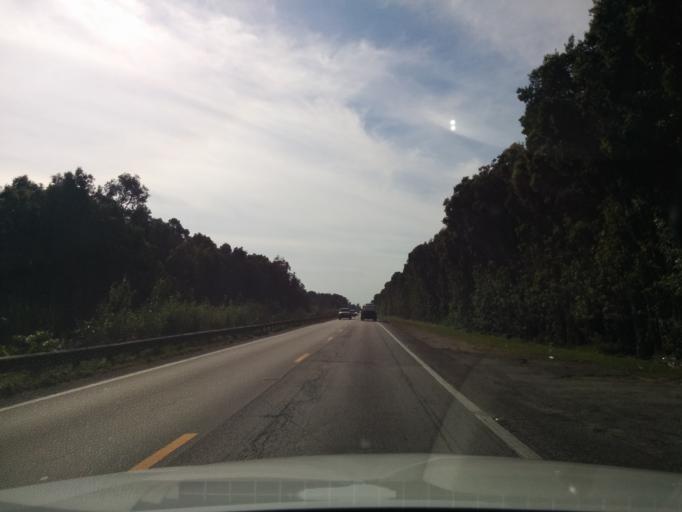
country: US
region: Florida
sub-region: Miami-Dade County
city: Kendall West
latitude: 25.7379
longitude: -80.4805
